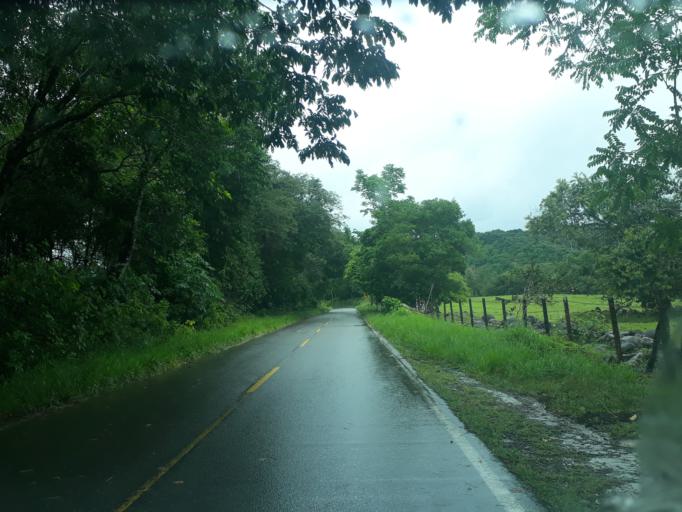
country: CO
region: Cundinamarca
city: Medina
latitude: 4.4550
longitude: -73.3249
